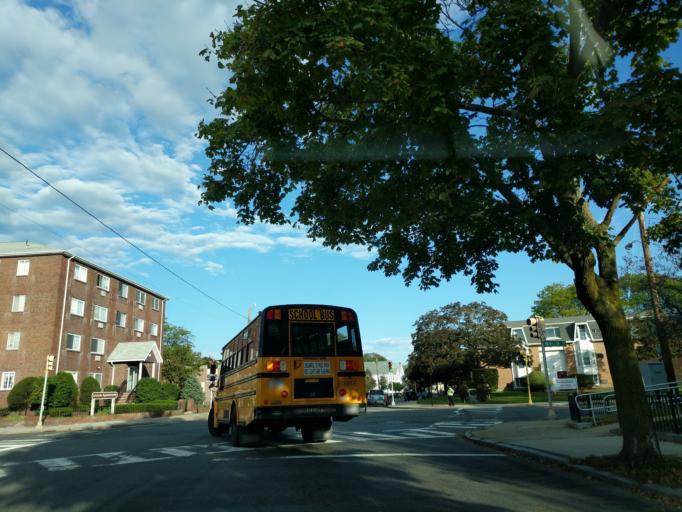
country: US
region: Massachusetts
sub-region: Middlesex County
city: Malden
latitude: 42.4256
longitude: -71.0545
